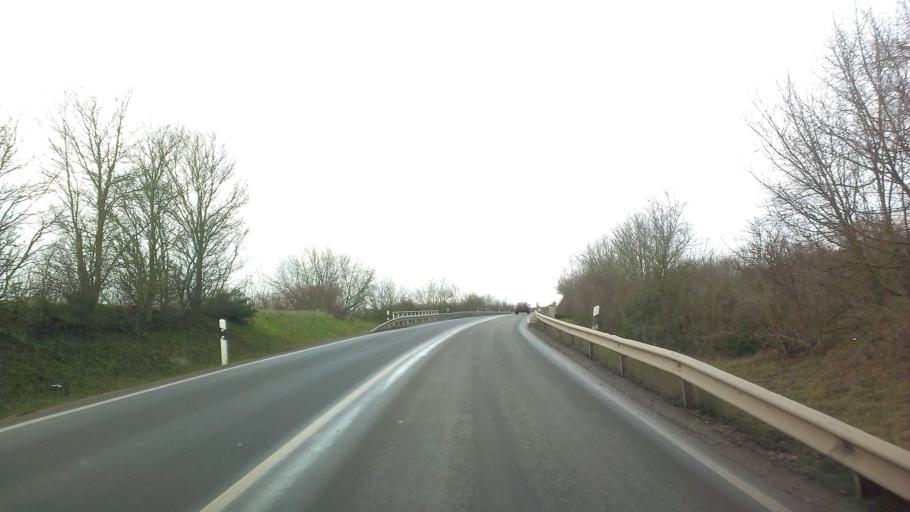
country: DE
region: Rheinland-Pfalz
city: Alzey
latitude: 49.7477
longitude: 8.0901
